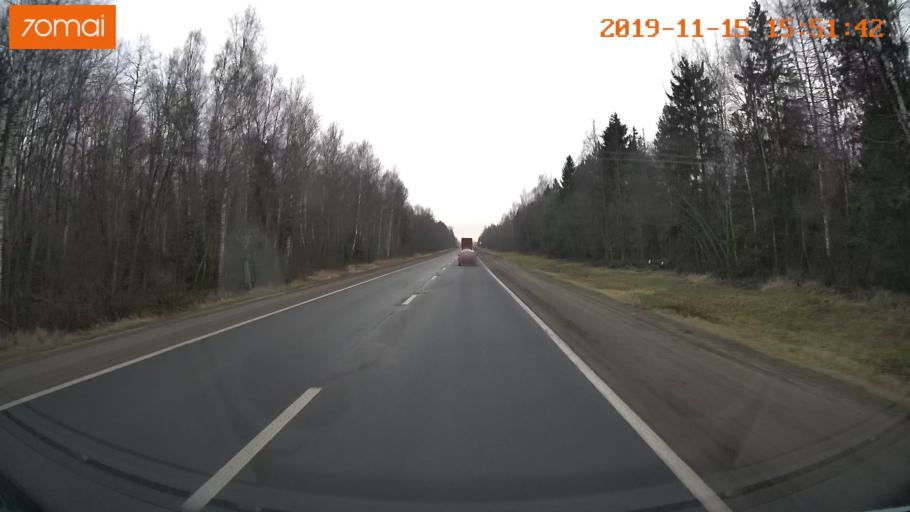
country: RU
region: Jaroslavl
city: Yaroslavl
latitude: 57.8913
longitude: 40.0054
